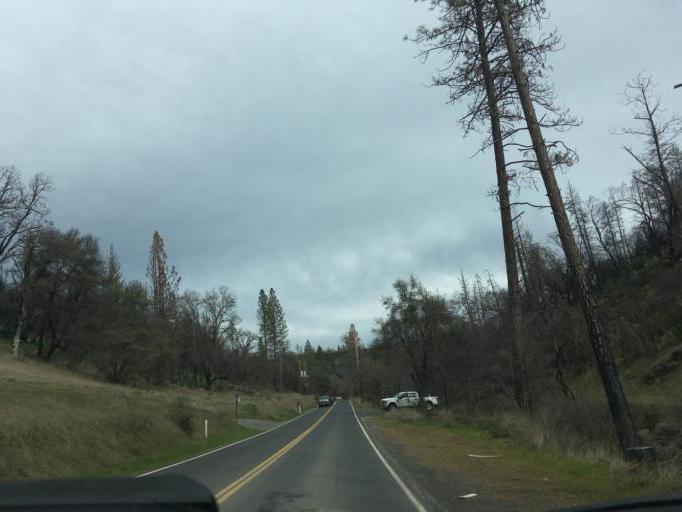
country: US
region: California
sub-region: Calaveras County
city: Mountain Ranch
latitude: 38.1982
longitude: -120.5834
